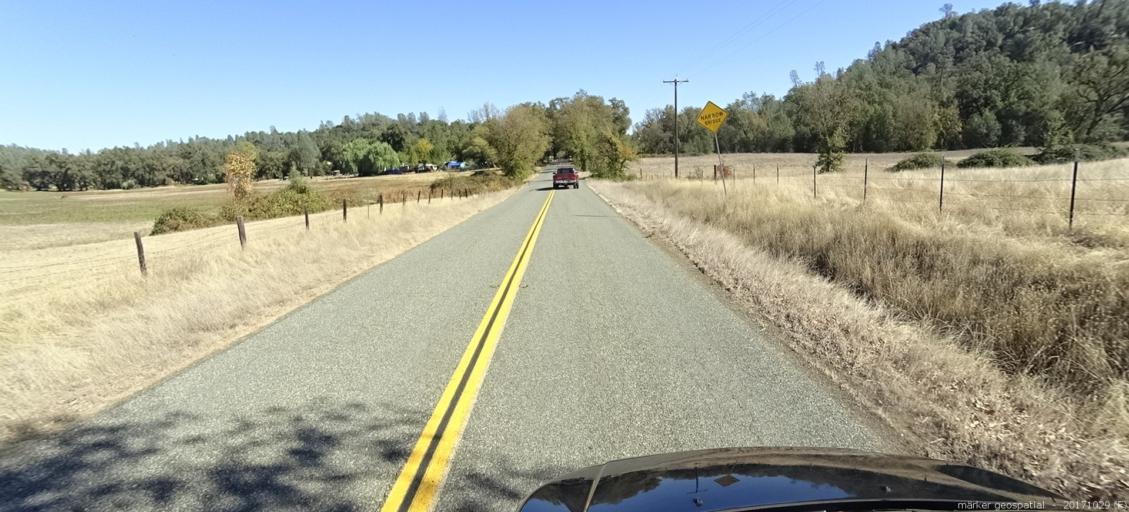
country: US
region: California
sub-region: Shasta County
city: Shasta
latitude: 40.4795
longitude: -122.5909
